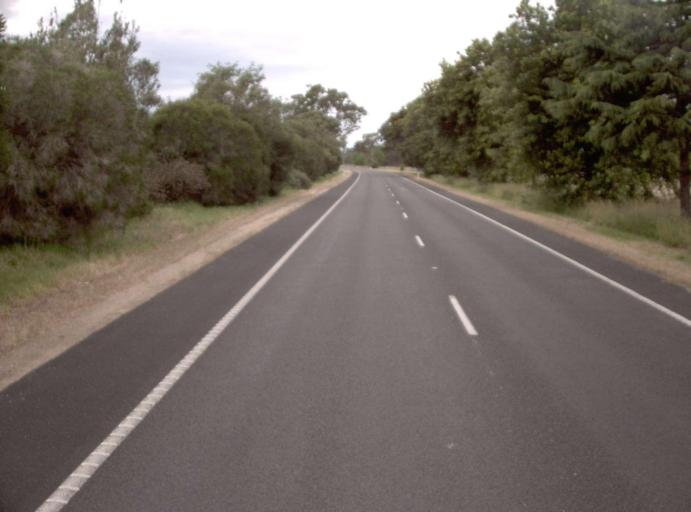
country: AU
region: Victoria
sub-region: East Gippsland
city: Bairnsdale
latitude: -37.8733
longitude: 147.6515
